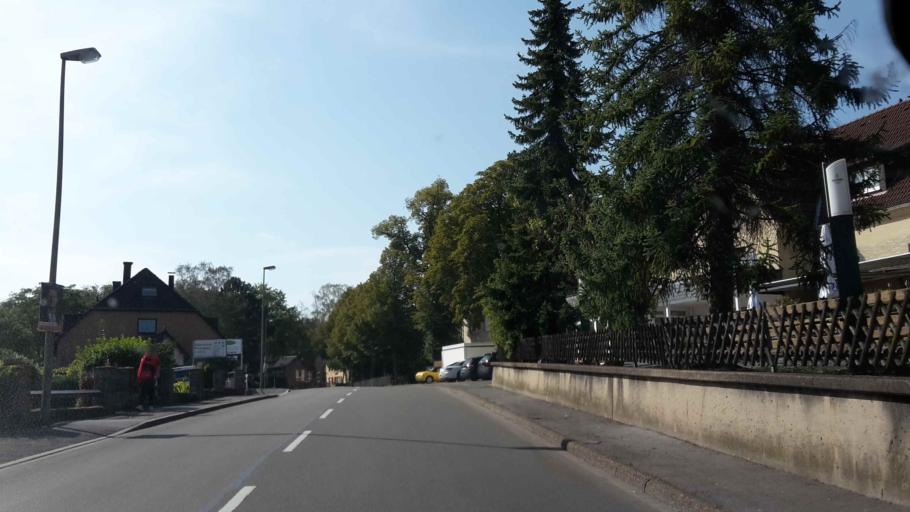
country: DE
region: North Rhine-Westphalia
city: Schwerte
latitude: 51.4441
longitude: 7.5271
